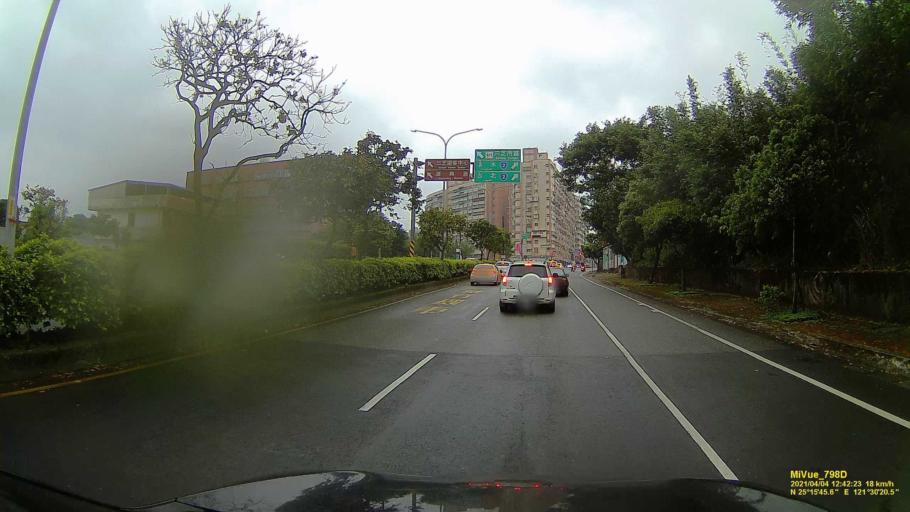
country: TW
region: Taipei
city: Taipei
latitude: 25.2626
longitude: 121.5057
